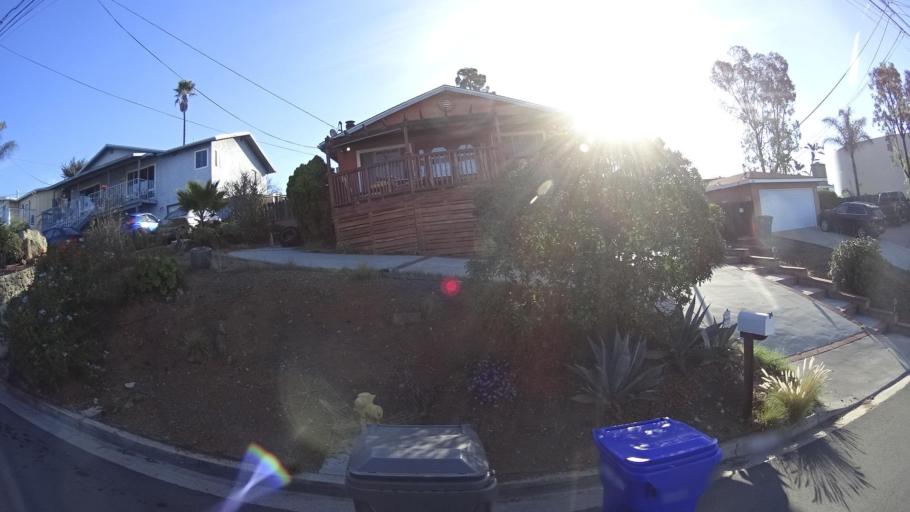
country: US
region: California
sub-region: San Diego County
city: La Presa
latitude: 32.7167
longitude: -116.9864
